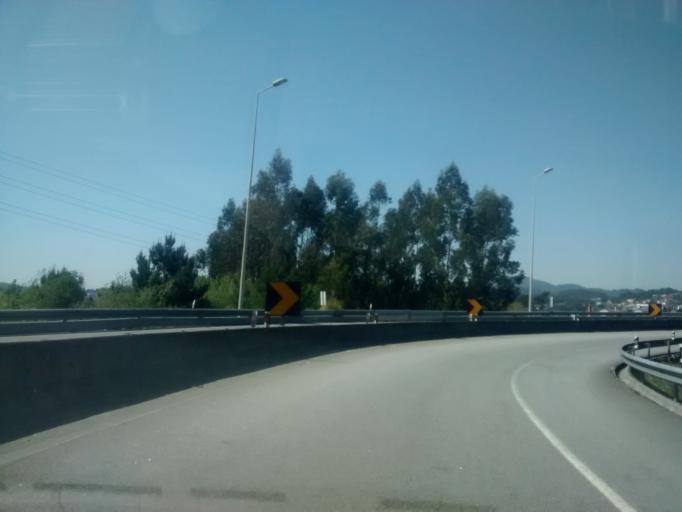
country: PT
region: Braga
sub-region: Braga
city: Braga
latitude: 41.5161
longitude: -8.4451
